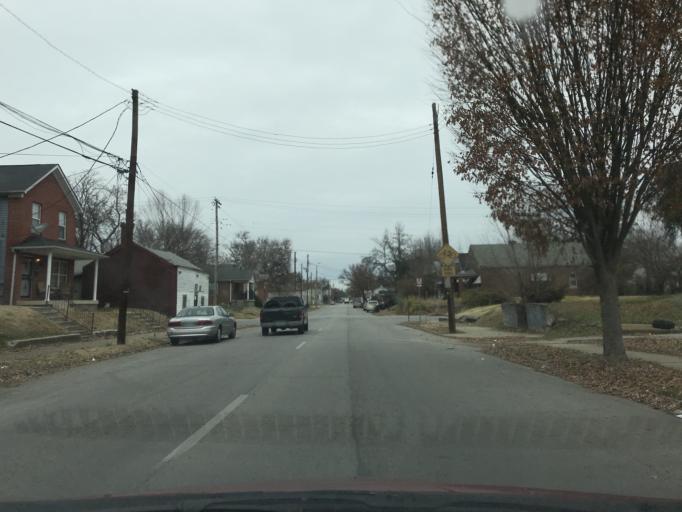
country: US
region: Kentucky
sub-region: Jefferson County
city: Louisville
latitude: 38.2552
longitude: -85.7855
